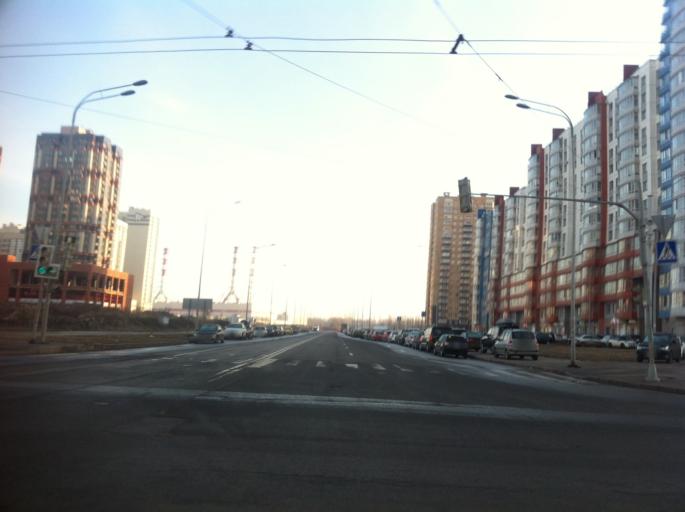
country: RU
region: St.-Petersburg
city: Uritsk
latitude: 59.8614
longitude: 30.1797
